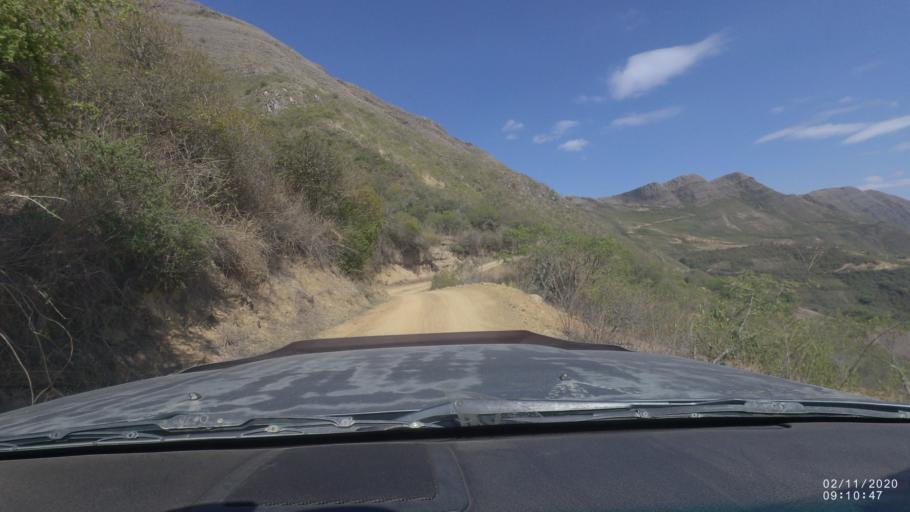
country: BO
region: Chuquisaca
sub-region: Provincia Zudanez
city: Mojocoya
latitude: -18.5148
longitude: -64.5673
